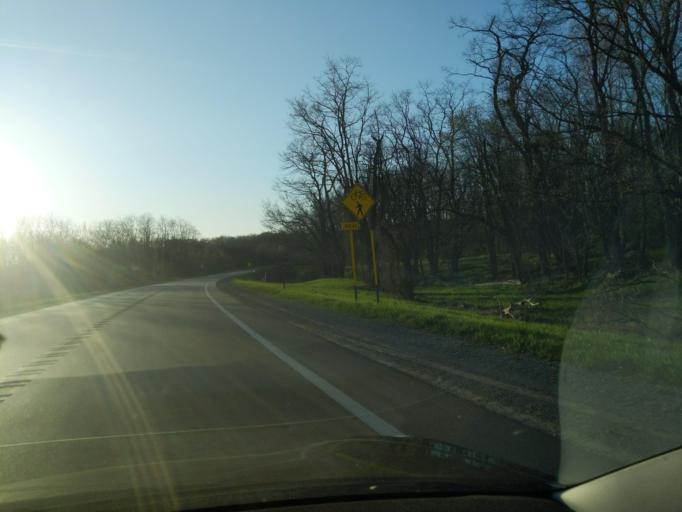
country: US
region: Michigan
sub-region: Washtenaw County
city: Chelsea
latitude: 42.3733
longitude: -84.0754
